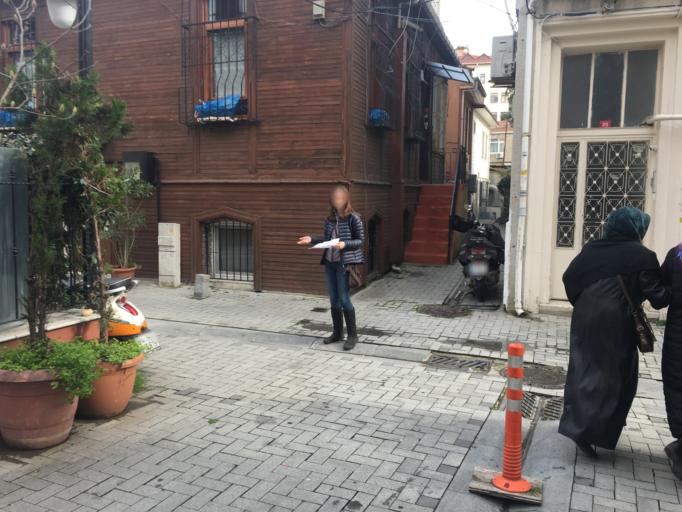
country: TR
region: Istanbul
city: UEskuedar
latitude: 41.0689
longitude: 29.0427
